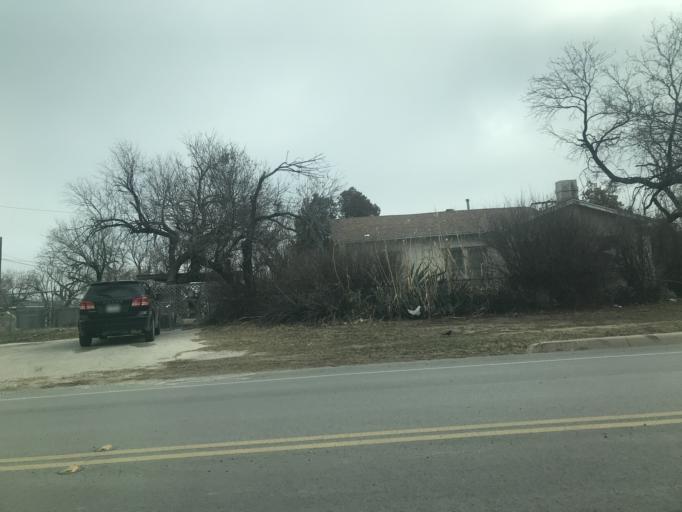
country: US
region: Texas
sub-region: Tom Green County
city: San Angelo
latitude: 31.4731
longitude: -100.4487
